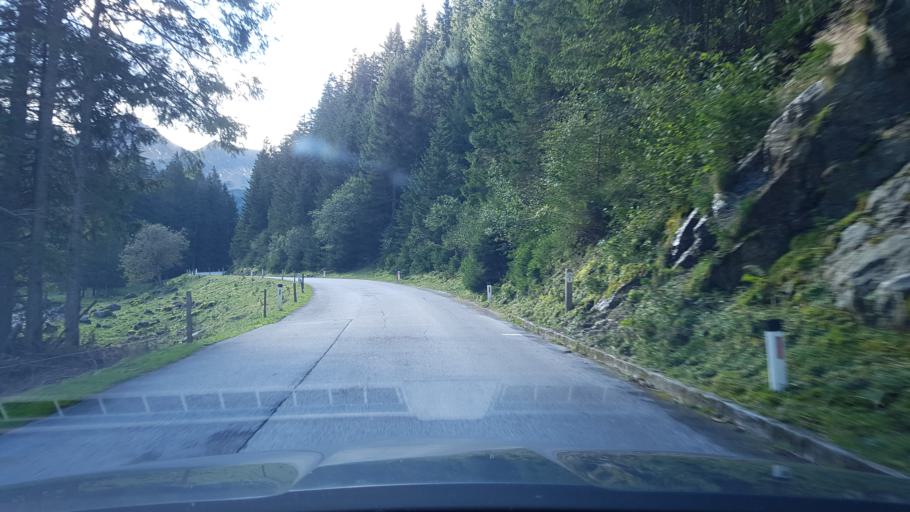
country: AT
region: Styria
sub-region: Politischer Bezirk Liezen
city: Sankt Nikolai im Solktal
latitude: 47.2979
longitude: 14.0736
